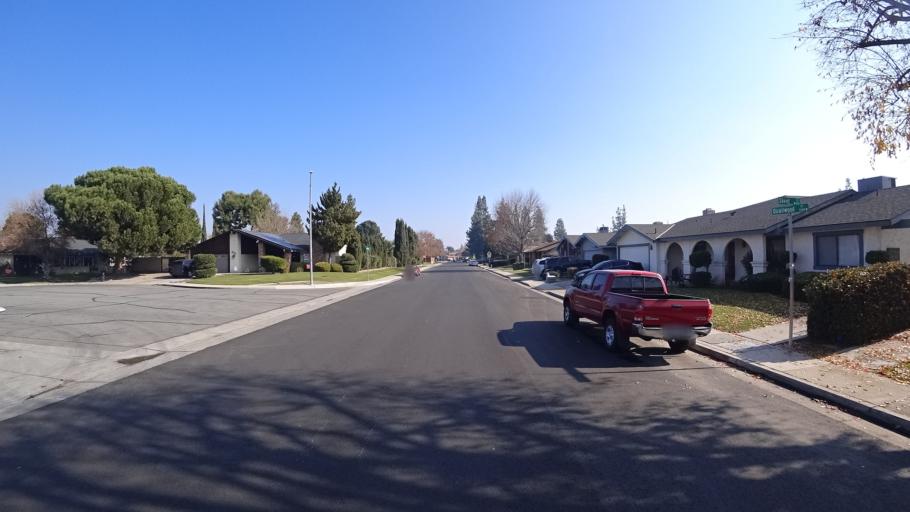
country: US
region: California
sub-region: Kern County
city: Greenacres
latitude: 35.3556
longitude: -119.0886
